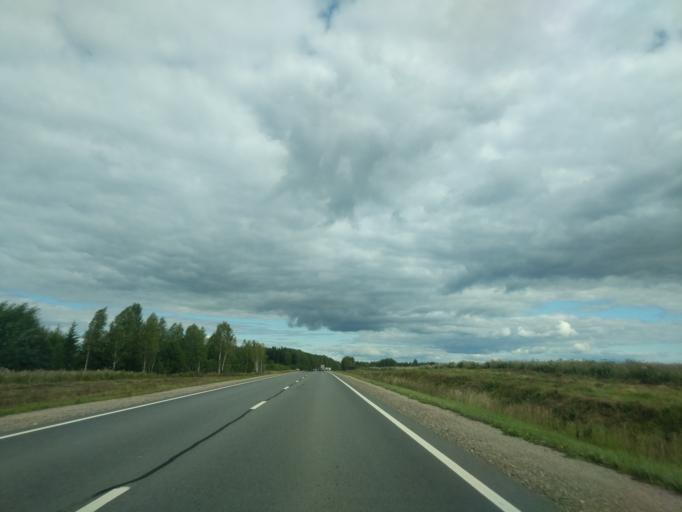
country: RU
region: Kostroma
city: Sudislavl'
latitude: 57.8170
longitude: 41.9535
